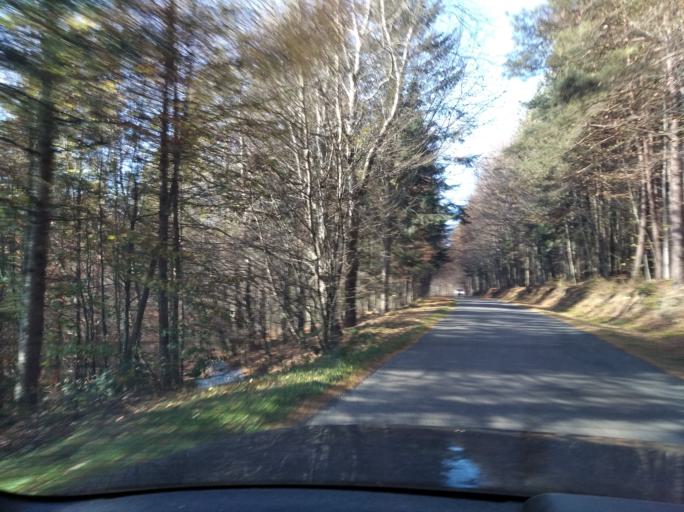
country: PL
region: Subcarpathian Voivodeship
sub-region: Powiat ropczycko-sedziszowski
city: Wielopole Skrzynskie
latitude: 49.8954
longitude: 21.5970
